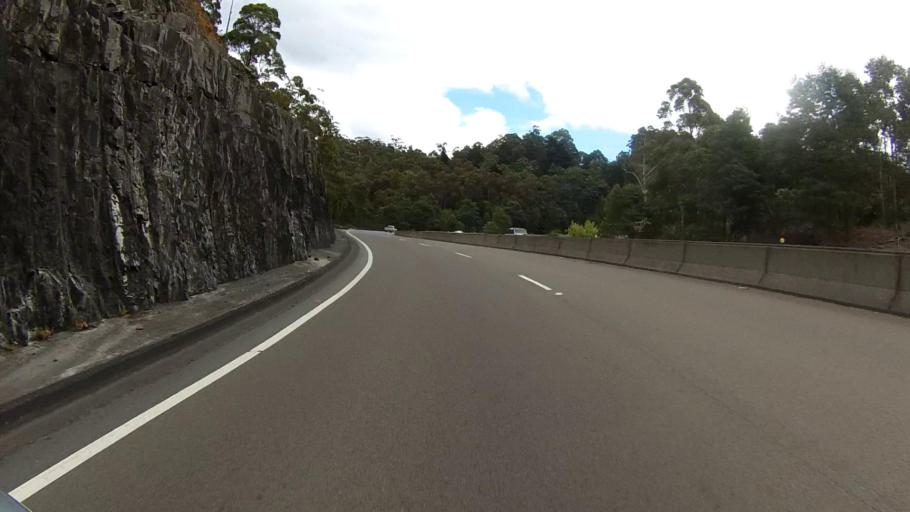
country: AU
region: Tasmania
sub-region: Kingborough
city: Margate
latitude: -42.9811
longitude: 147.1759
